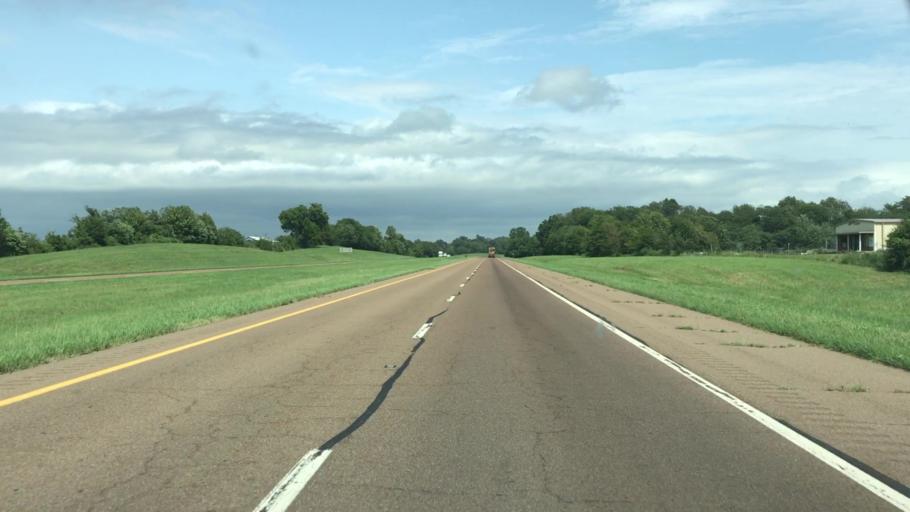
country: US
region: Tennessee
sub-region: Obion County
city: South Fulton
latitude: 36.4902
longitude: -88.9236
